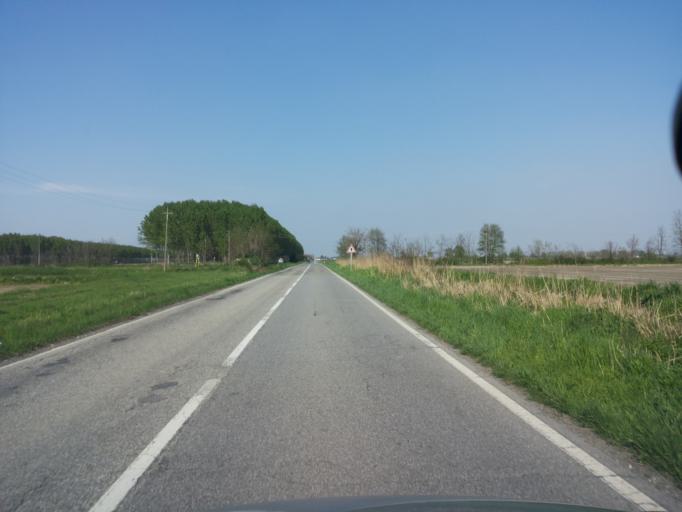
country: IT
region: Lombardy
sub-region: Provincia di Pavia
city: Zeme
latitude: 45.2139
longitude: 8.6527
